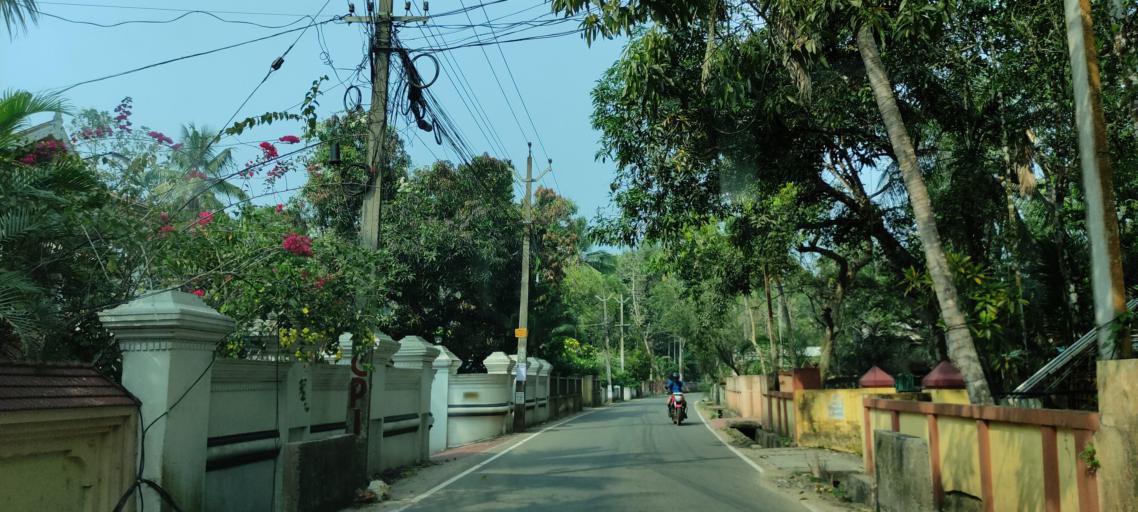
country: IN
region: Kerala
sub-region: Kottayam
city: Vaikam
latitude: 9.7571
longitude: 76.4019
